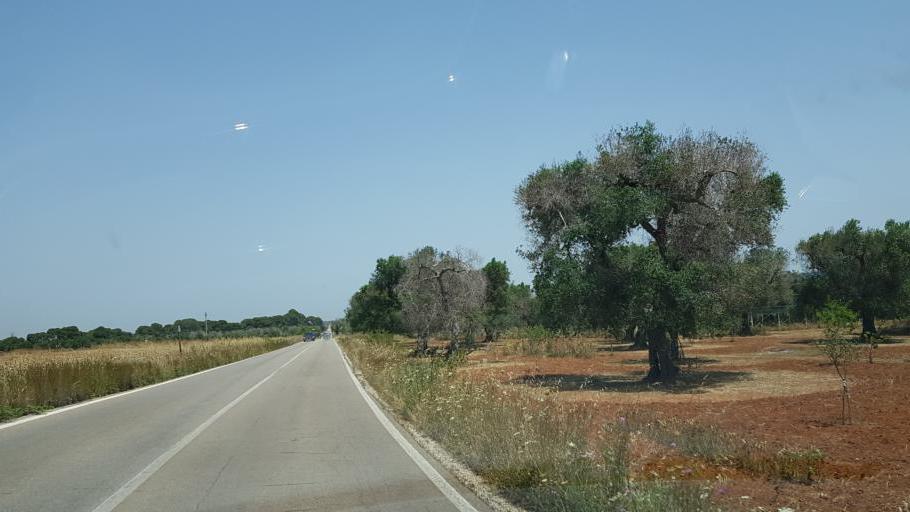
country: IT
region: Apulia
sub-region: Provincia di Lecce
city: Porto Cesareo
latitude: 40.3026
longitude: 17.9176
